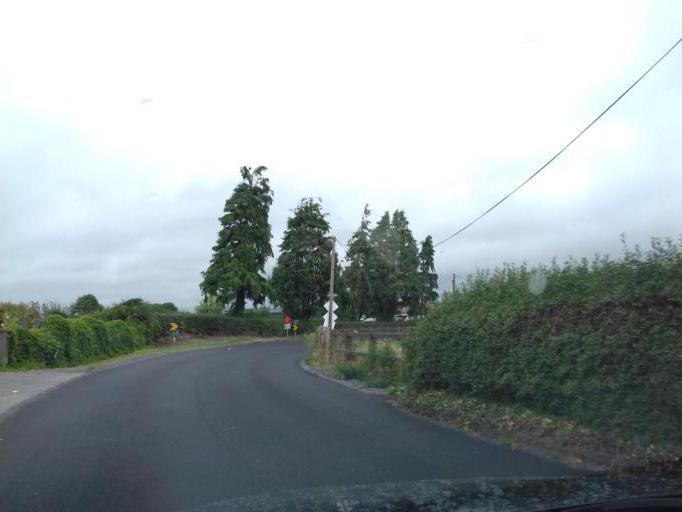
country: IE
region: Leinster
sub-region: Kilkenny
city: Graiguenamanagh
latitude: 52.6073
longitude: -7.0233
